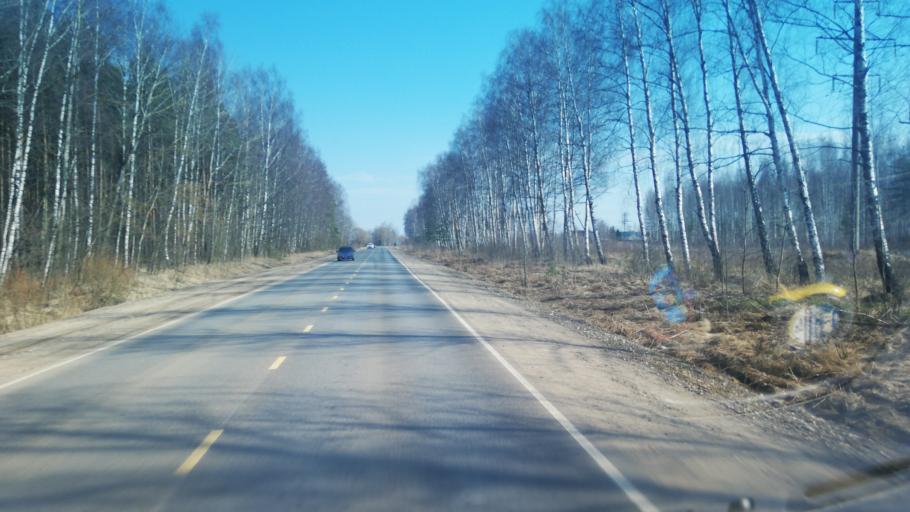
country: RU
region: Jaroslavl
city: Rostov
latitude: 57.2351
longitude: 39.4833
